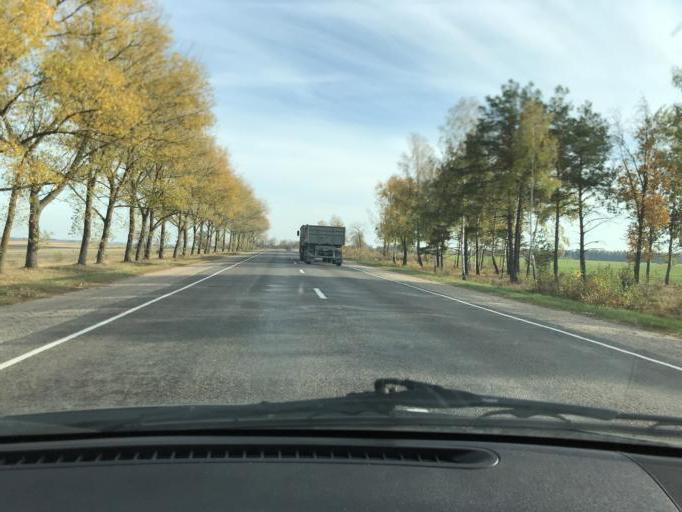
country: BY
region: Brest
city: Lahishyn
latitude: 52.2417
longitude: 25.9992
